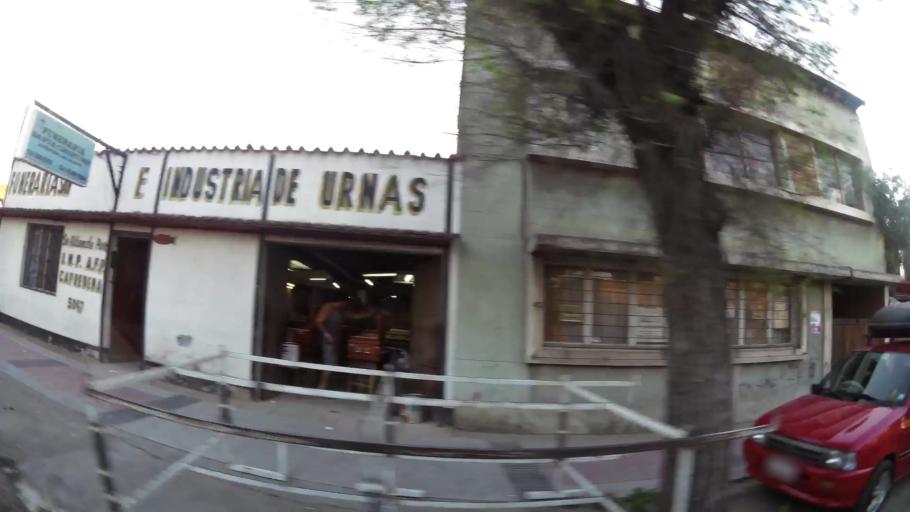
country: CL
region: Santiago Metropolitan
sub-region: Provincia de Santiago
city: Santiago
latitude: -33.5033
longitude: -70.6334
